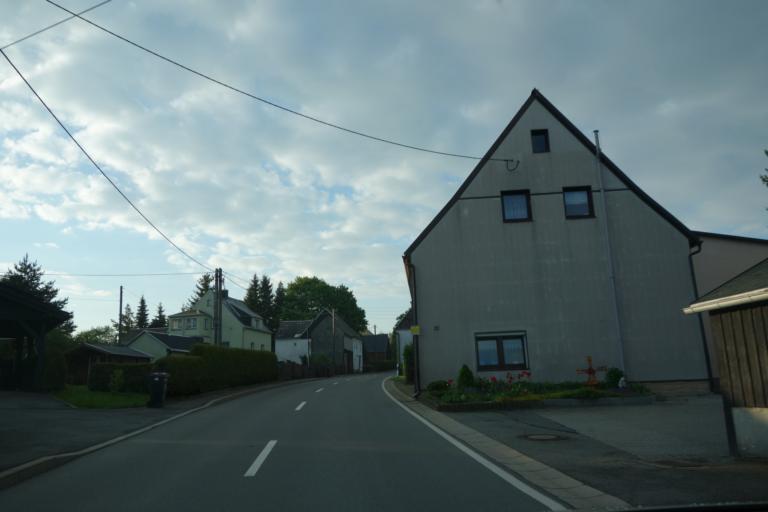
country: DE
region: Saxony
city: Zoblitz
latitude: 50.6441
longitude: 13.2623
